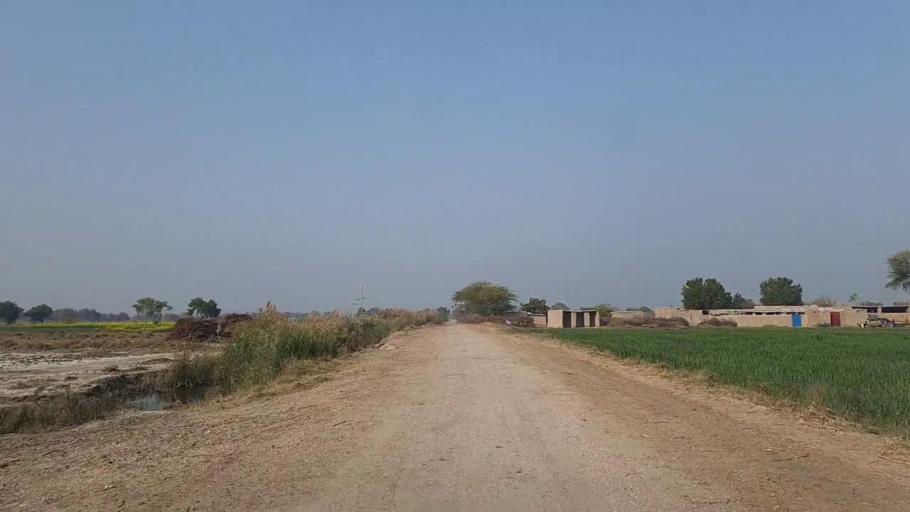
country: PK
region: Sindh
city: Nawabshah
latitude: 26.3490
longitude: 68.4740
